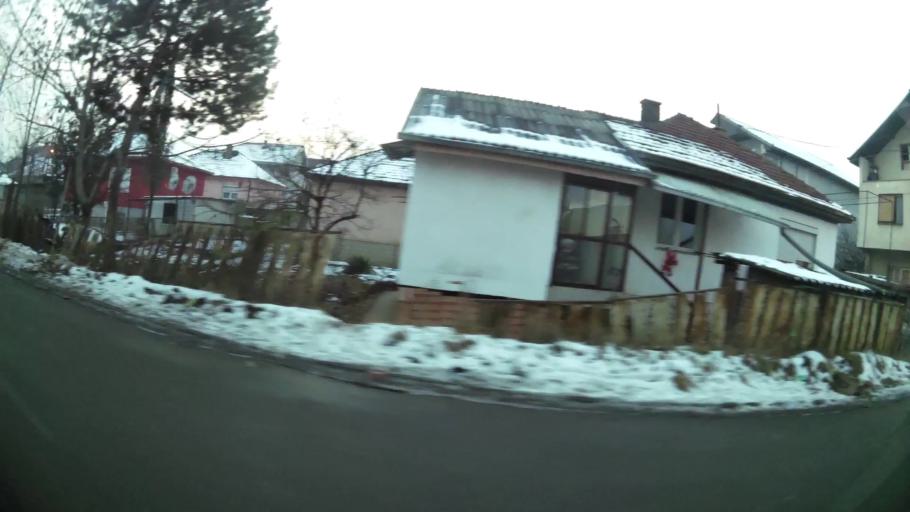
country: MK
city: Creshevo
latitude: 42.0128
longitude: 21.5164
